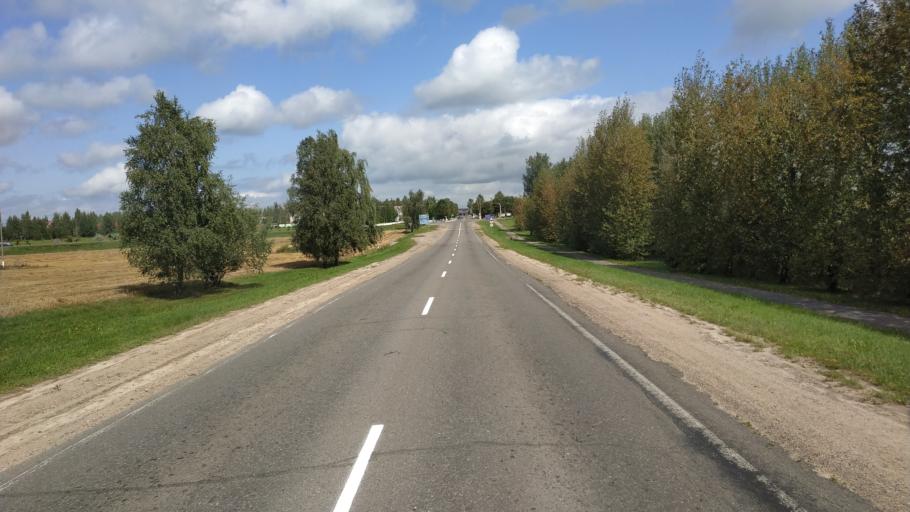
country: BY
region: Mogilev
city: Chavusy
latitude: 53.7997
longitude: 30.9507
